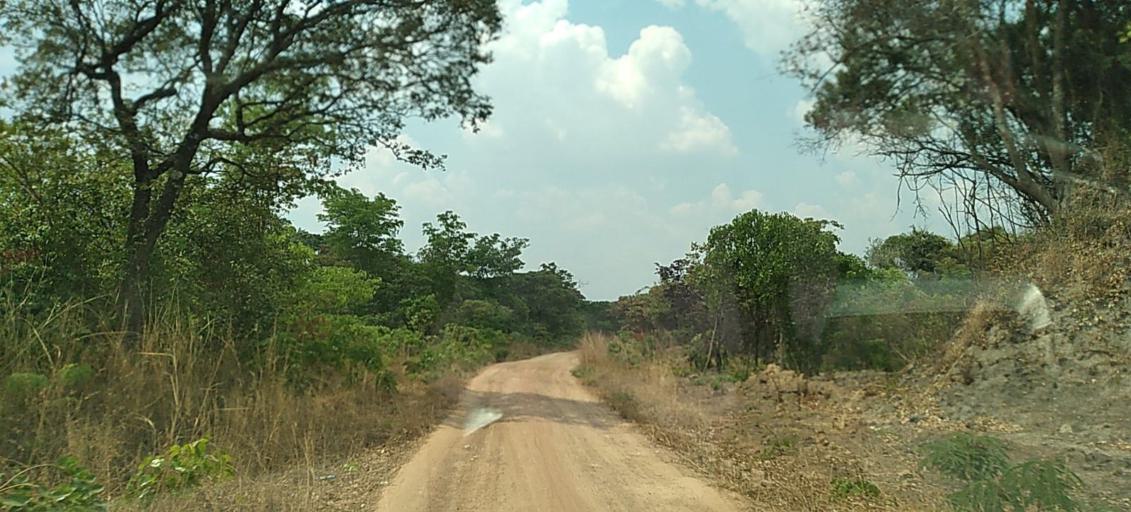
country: ZM
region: Copperbelt
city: Chingola
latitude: -12.6805
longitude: 27.7225
